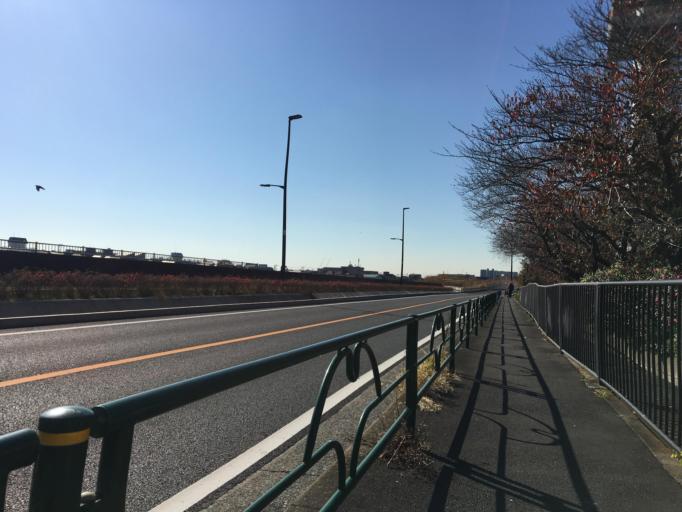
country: JP
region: Tokyo
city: Urayasu
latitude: 35.6850
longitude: 139.9065
